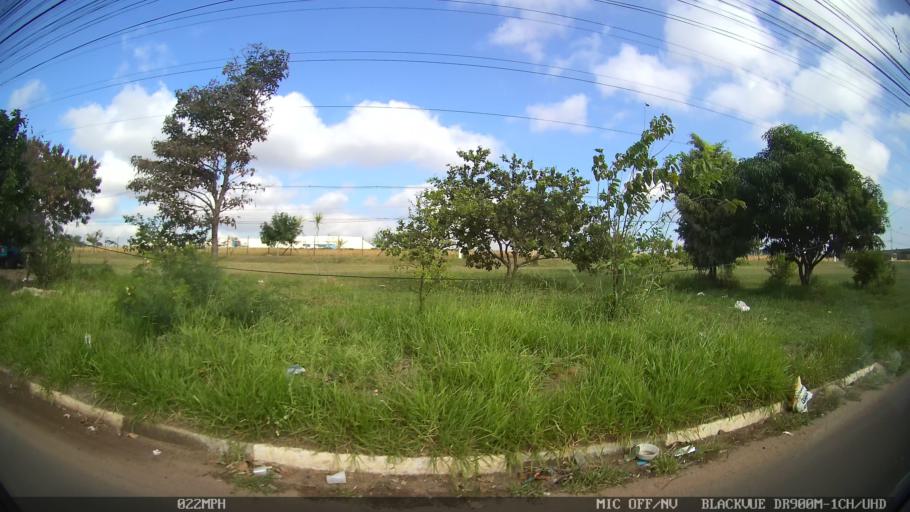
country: BR
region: Sao Paulo
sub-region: Hortolandia
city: Hortolandia
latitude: -22.9077
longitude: -47.1830
